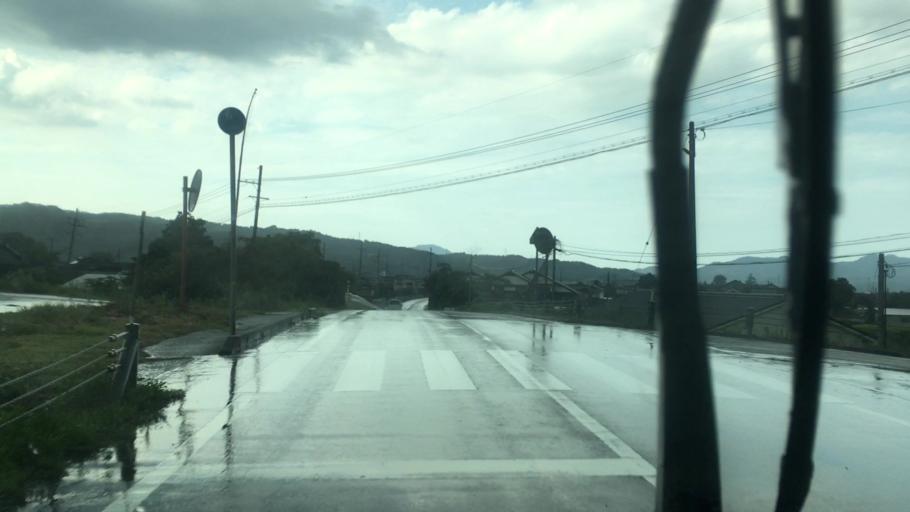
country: JP
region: Hyogo
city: Toyooka
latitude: 35.4886
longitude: 134.8165
